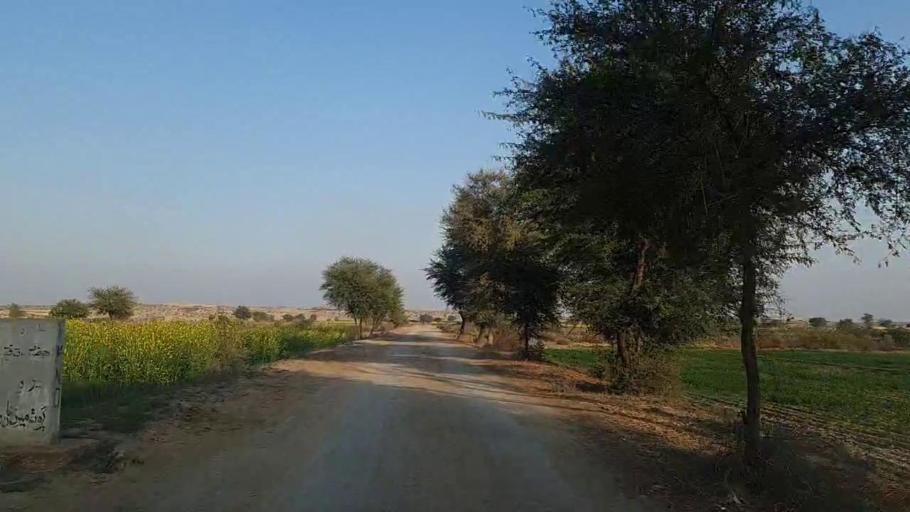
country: PK
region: Sindh
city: Jam Sahib
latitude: 26.3906
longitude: 68.5410
